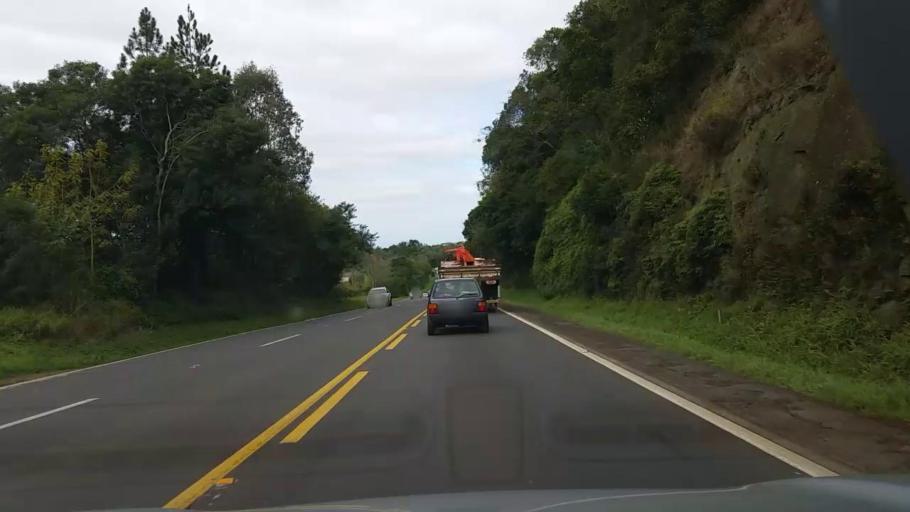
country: BR
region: Rio Grande do Sul
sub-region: Arroio Do Meio
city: Arroio do Meio
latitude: -29.3971
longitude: -52.0418
